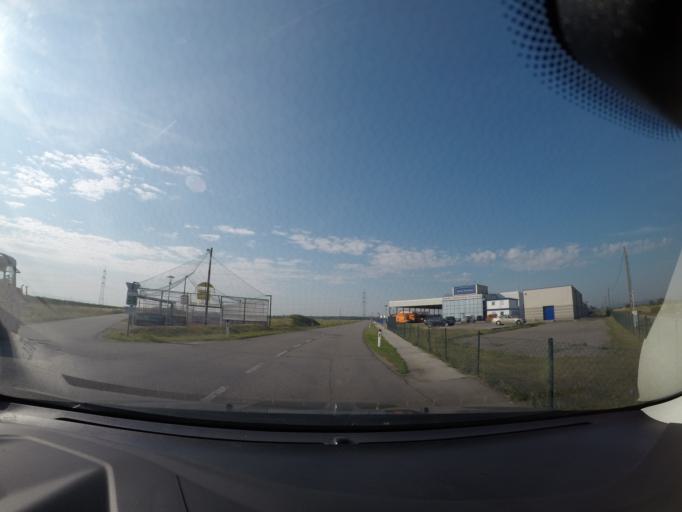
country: AT
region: Lower Austria
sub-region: Politischer Bezirk Baden
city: Teesdorf
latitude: 47.9422
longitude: 16.2895
